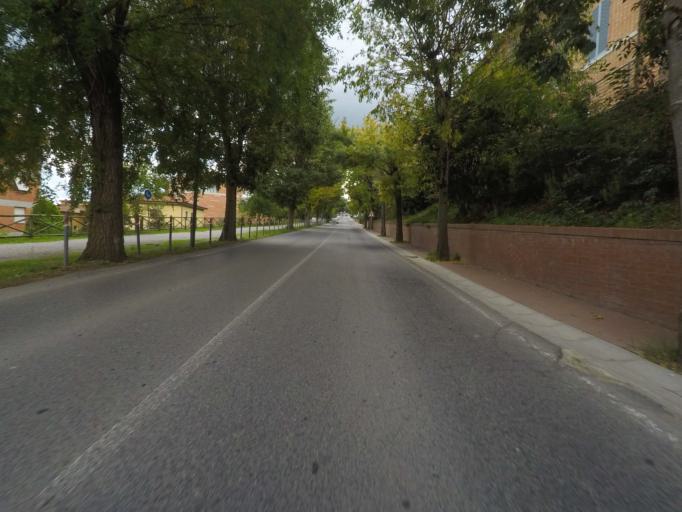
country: IT
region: Tuscany
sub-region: Provincia di Siena
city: Montepulciano
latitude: 43.1022
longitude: 11.7856
